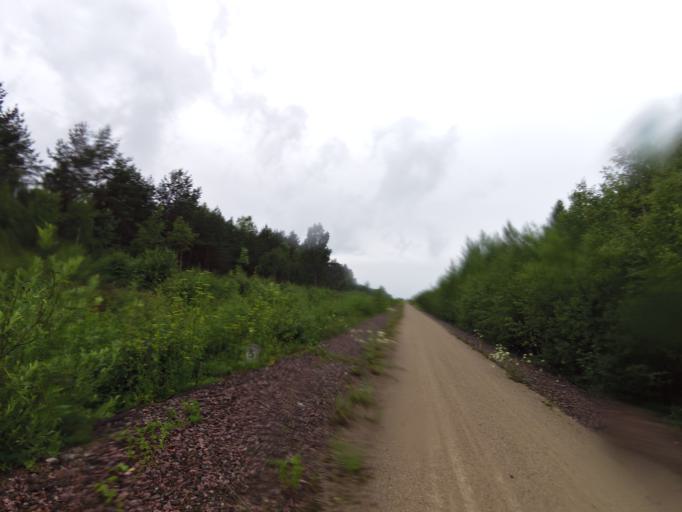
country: EE
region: Laeaene
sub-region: Ridala Parish
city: Uuemoisa
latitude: 58.9555
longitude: 23.8375
